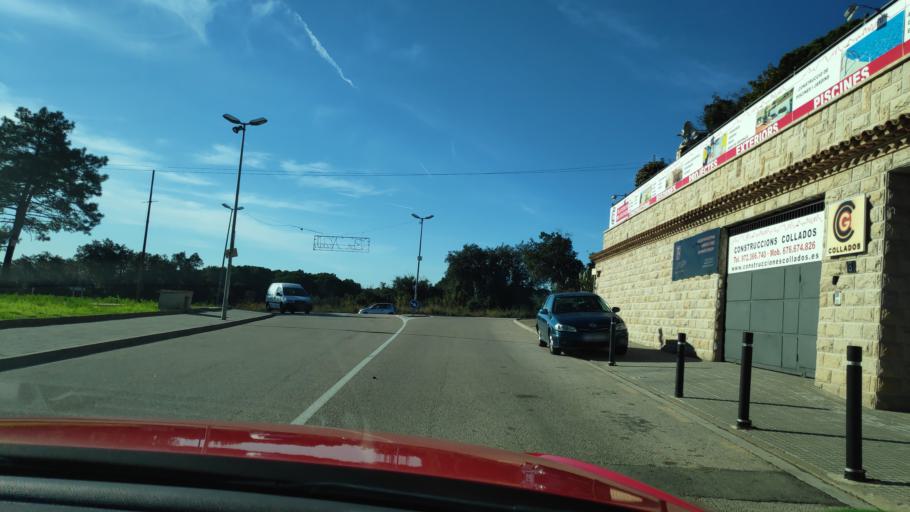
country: ES
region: Catalonia
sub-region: Provincia de Girona
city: Lloret de Mar
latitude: 41.7234
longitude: 2.8254
